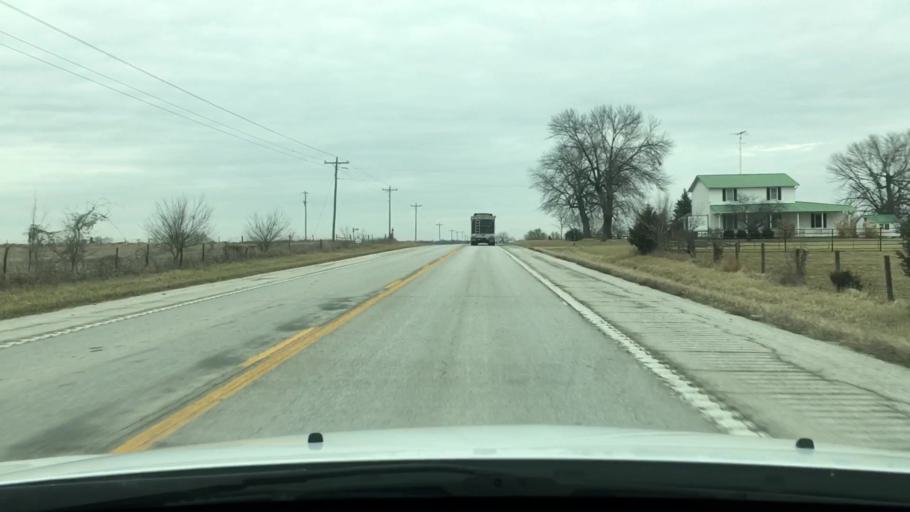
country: US
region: Missouri
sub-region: Montgomery County
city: Wellsville
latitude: 39.1762
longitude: -91.6475
